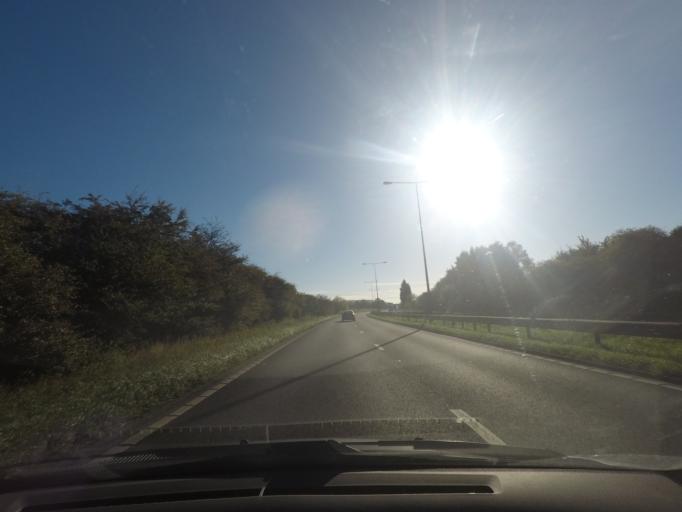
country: GB
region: England
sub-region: East Riding of Yorkshire
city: South Cave
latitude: 53.7601
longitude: -0.5924
